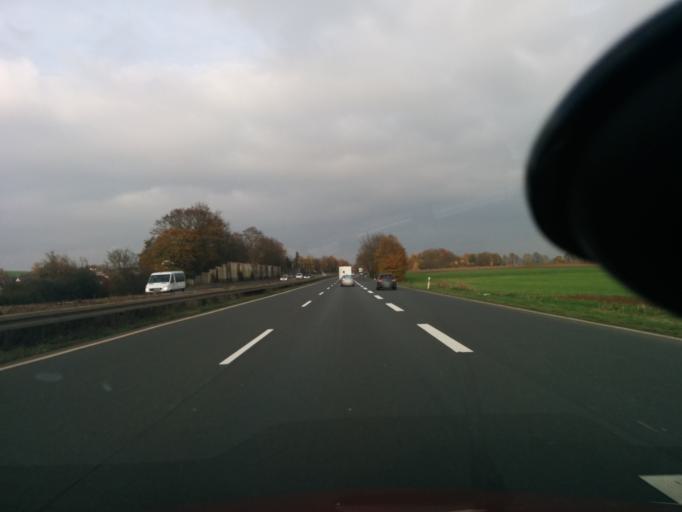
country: DE
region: Hesse
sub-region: Regierungsbezirk Giessen
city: Dehrn
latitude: 50.4335
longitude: 8.0914
